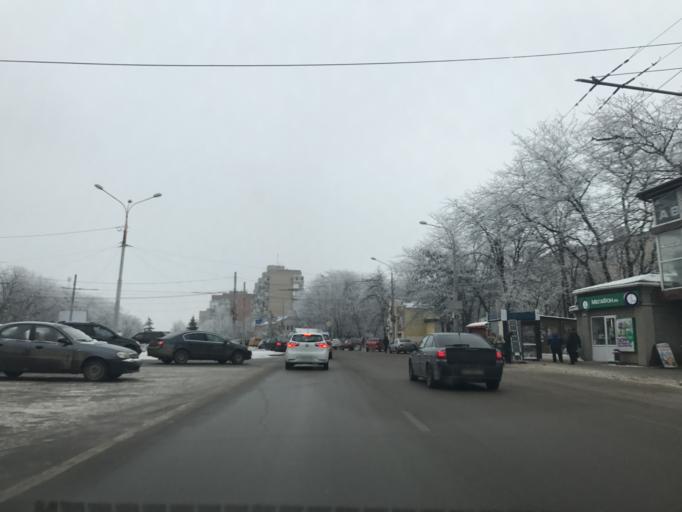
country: RU
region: Rostov
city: Aksay
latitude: 47.2389
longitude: 39.8300
